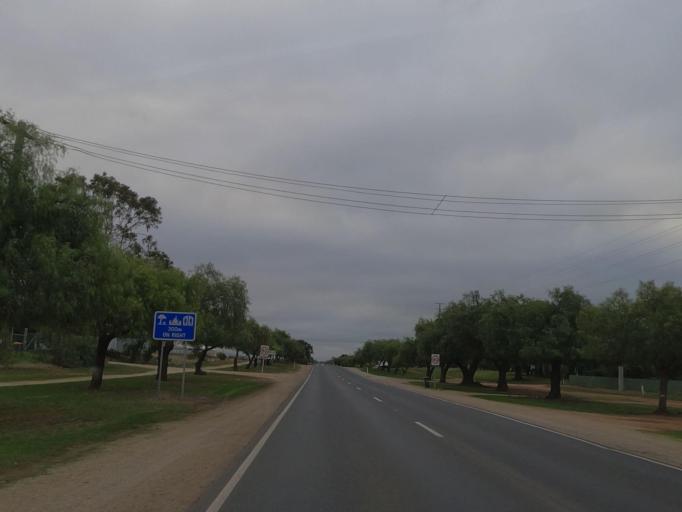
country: AU
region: Victoria
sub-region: Swan Hill
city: Swan Hill
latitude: -35.4563
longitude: 143.6294
